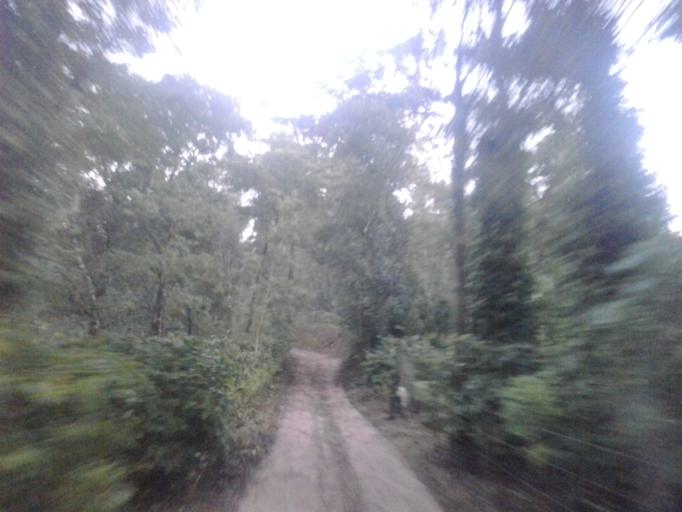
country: IN
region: Karnataka
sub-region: Chikmagalur
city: Mudigere
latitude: 13.0133
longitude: 75.6701
